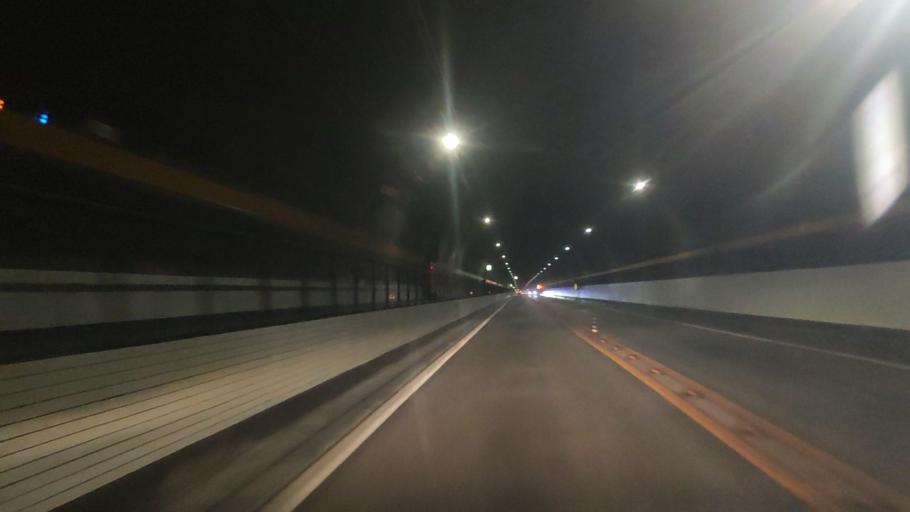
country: JP
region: Nagasaki
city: Obita
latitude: 32.7837
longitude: 129.8842
